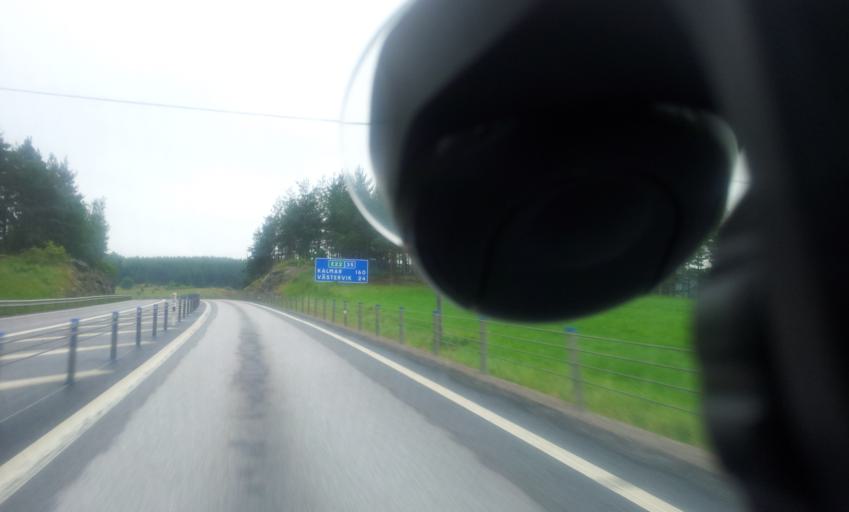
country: SE
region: Kalmar
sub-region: Vasterviks Kommun
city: Gamleby
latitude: 57.9027
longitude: 16.3830
